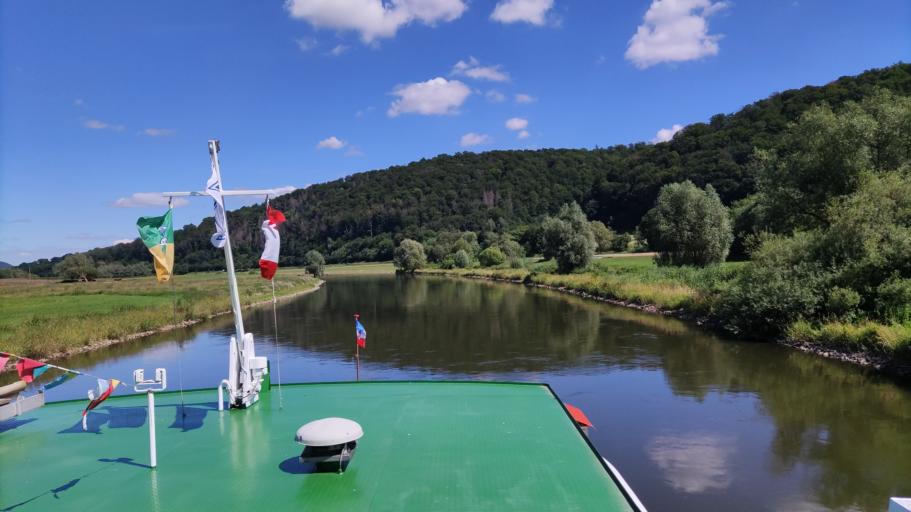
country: DE
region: Lower Saxony
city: Derental
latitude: 51.6994
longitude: 9.4011
